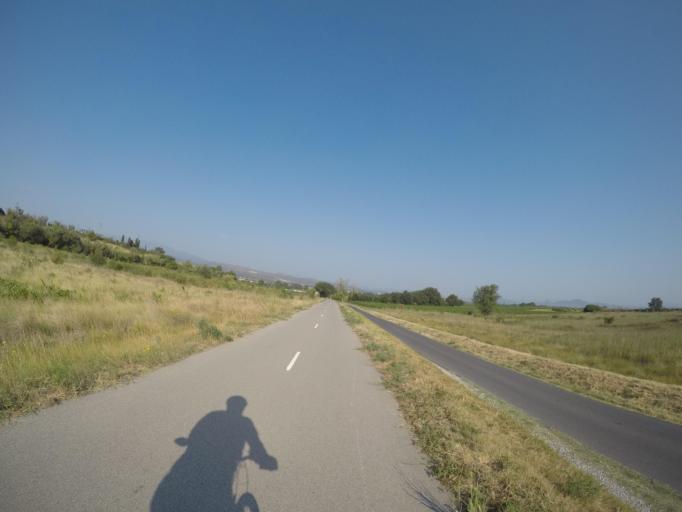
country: FR
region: Languedoc-Roussillon
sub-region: Departement des Pyrenees-Orientales
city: Trouillas
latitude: 42.6233
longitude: 2.7917
